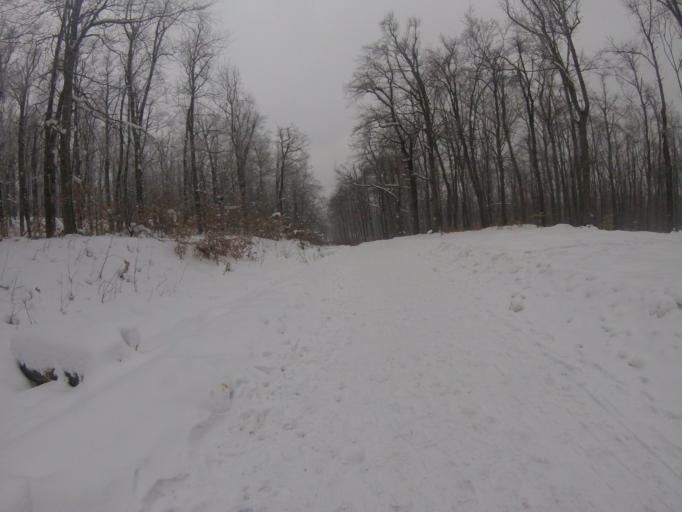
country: HU
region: Pest
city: Pilisszanto
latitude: 47.6967
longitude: 18.8636
